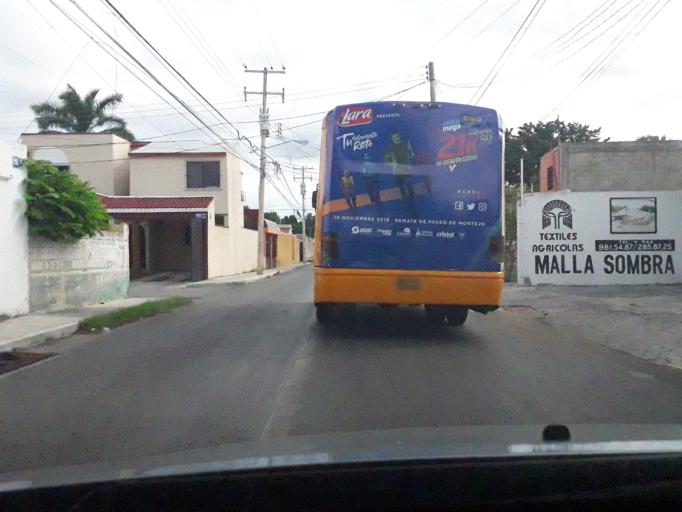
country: MX
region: Yucatan
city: Merida
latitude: 21.0169
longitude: -89.6319
